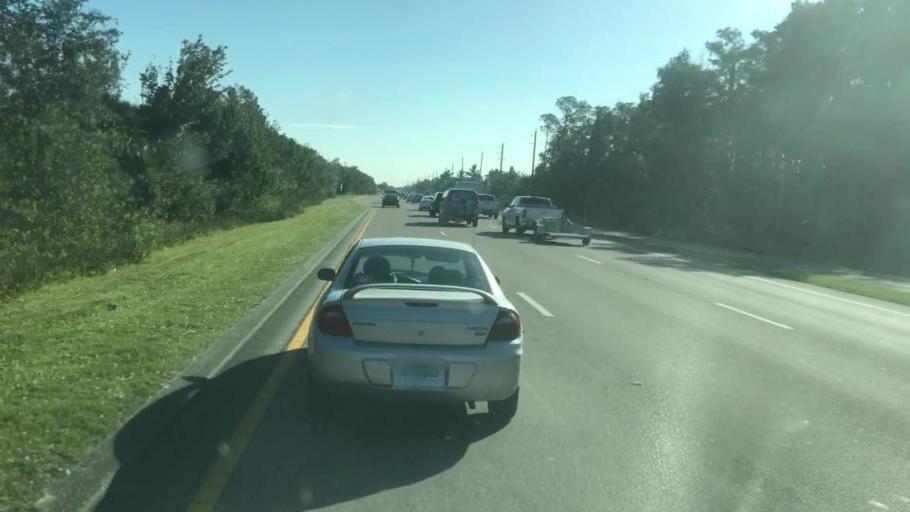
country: US
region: Florida
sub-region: Lee County
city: Villas
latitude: 26.5470
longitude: -81.8148
